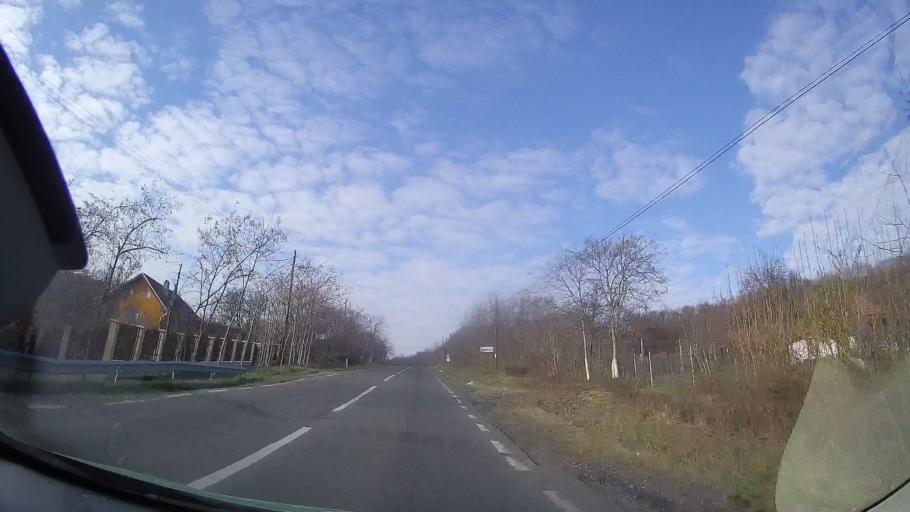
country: RO
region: Cluj
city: Jucu Herghelia
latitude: 46.8098
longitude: 23.8373
